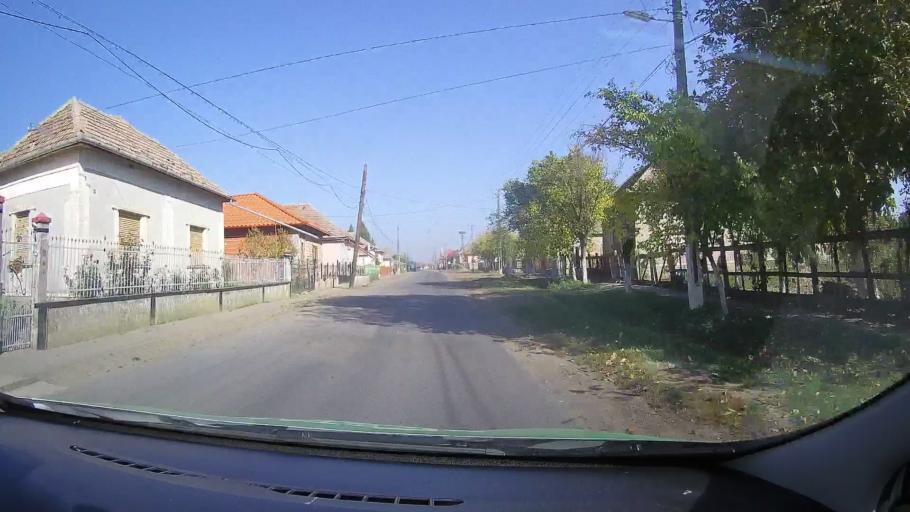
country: RO
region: Satu Mare
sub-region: Comuna Ciumesti
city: Ciumesti
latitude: 47.6578
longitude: 22.3339
